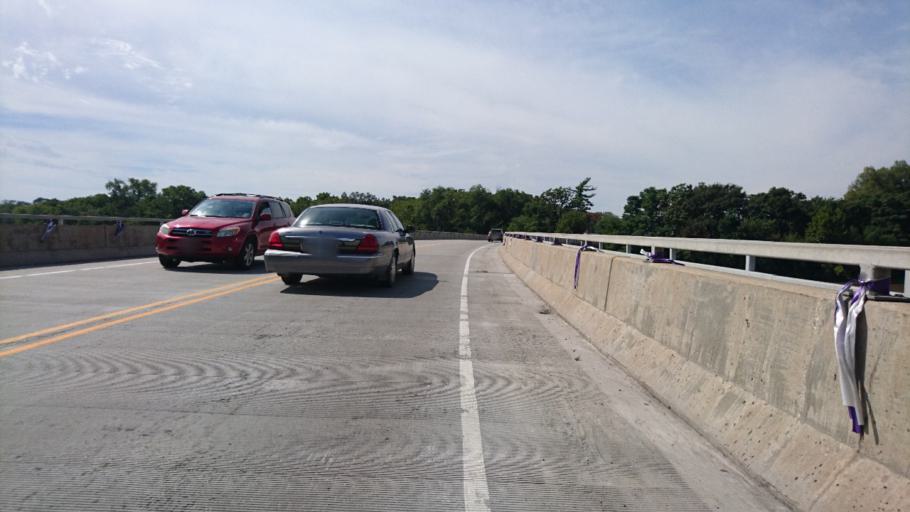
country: US
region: Illinois
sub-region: Will County
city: Wilmington
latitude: 41.3058
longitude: -88.1506
